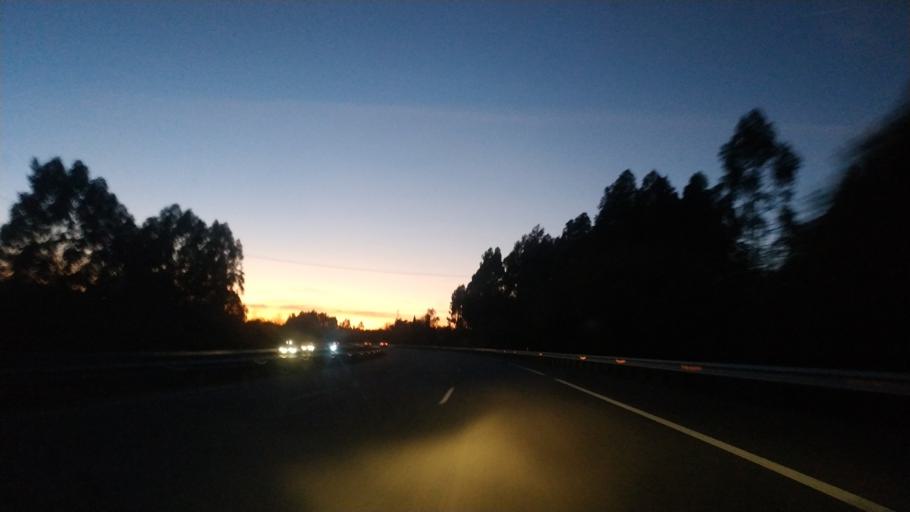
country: ES
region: Asturias
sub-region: Province of Asturias
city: Castrillon
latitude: 43.5456
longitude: -6.0157
